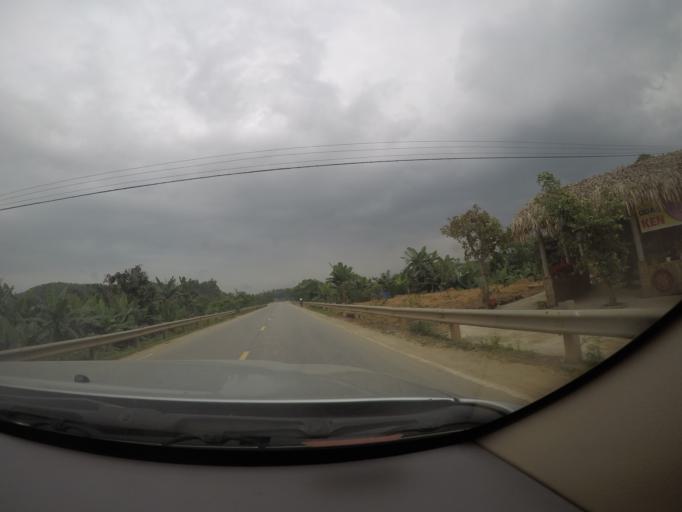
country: VN
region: Quang Binh
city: Ba Don
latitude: 17.6157
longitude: 106.3678
